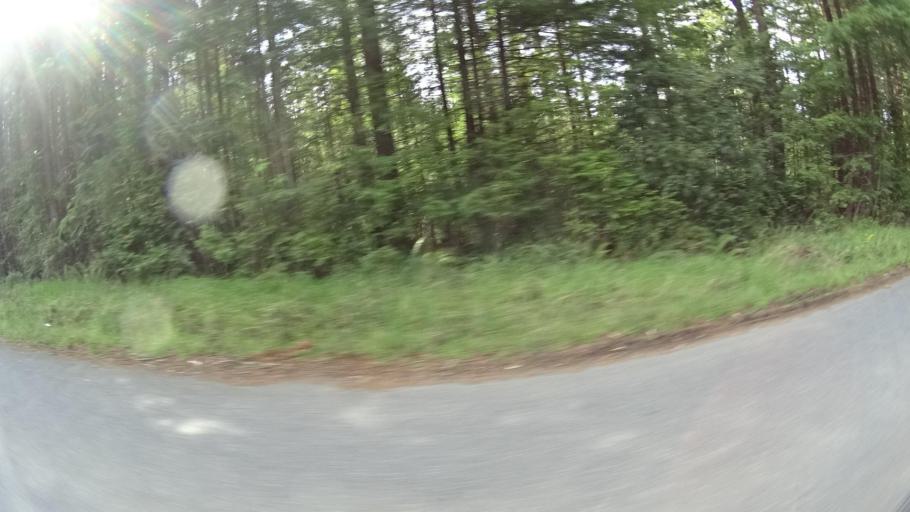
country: US
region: California
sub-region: Humboldt County
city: Bayside
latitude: 40.7597
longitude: -124.0092
